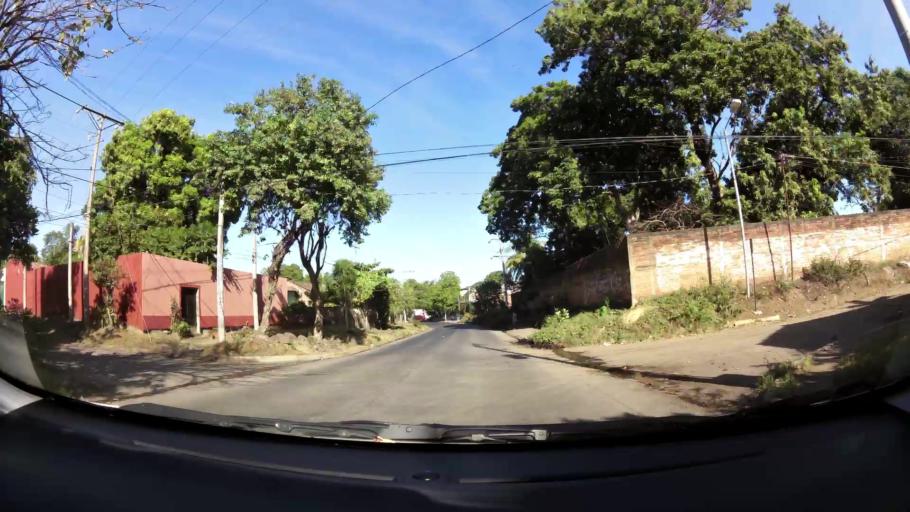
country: SV
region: San Miguel
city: San Miguel
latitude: 13.4783
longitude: -88.1908
